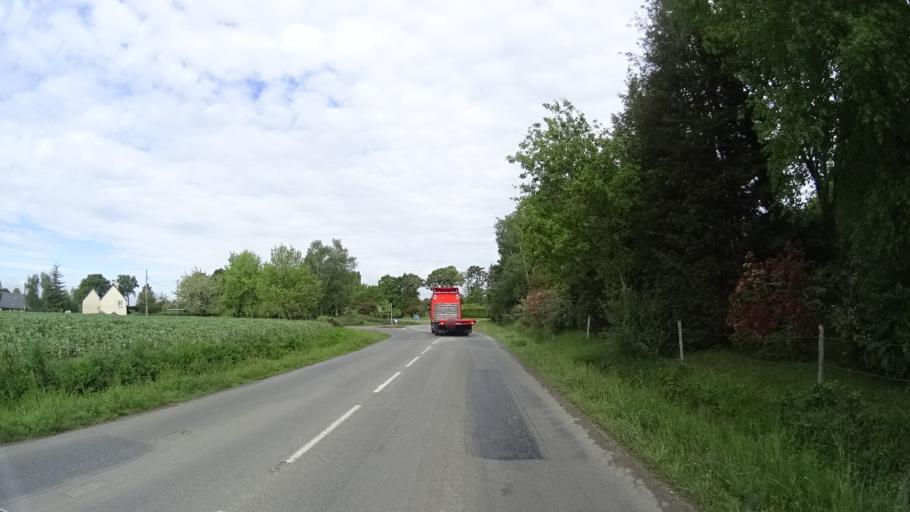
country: FR
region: Brittany
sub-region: Departement d'Ille-et-Vilaine
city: Mordelles
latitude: 48.0852
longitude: -1.8400
